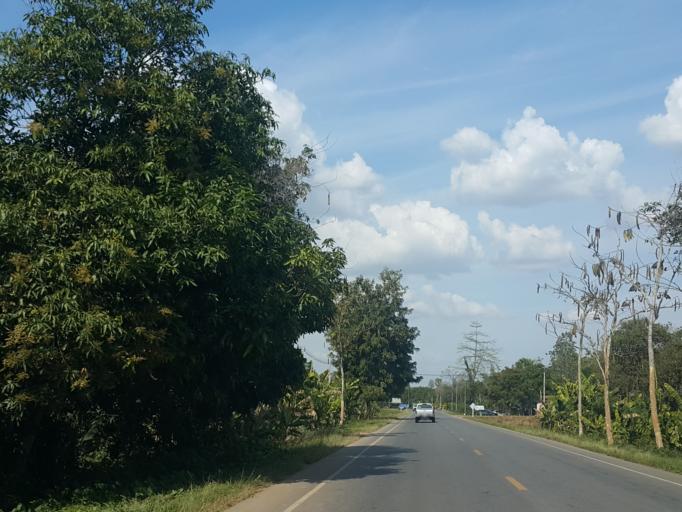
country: TH
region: Sukhothai
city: Sawankhalok
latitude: 17.2415
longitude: 99.8468
